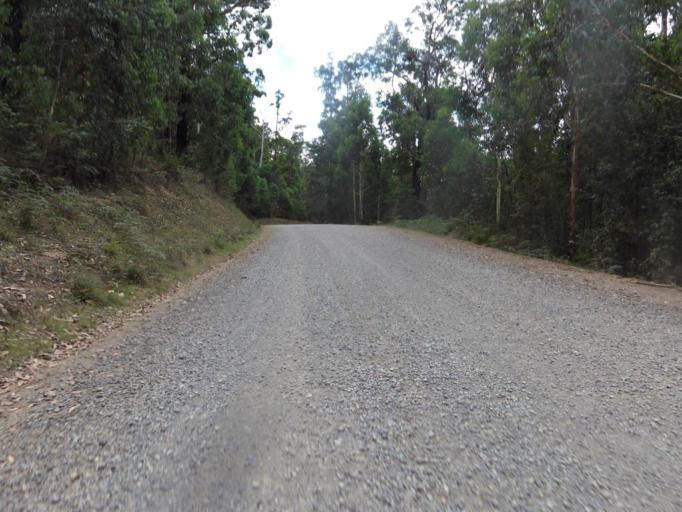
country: AU
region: Victoria
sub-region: Yarra Ranges
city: Healesville
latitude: -37.4074
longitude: 145.5589
